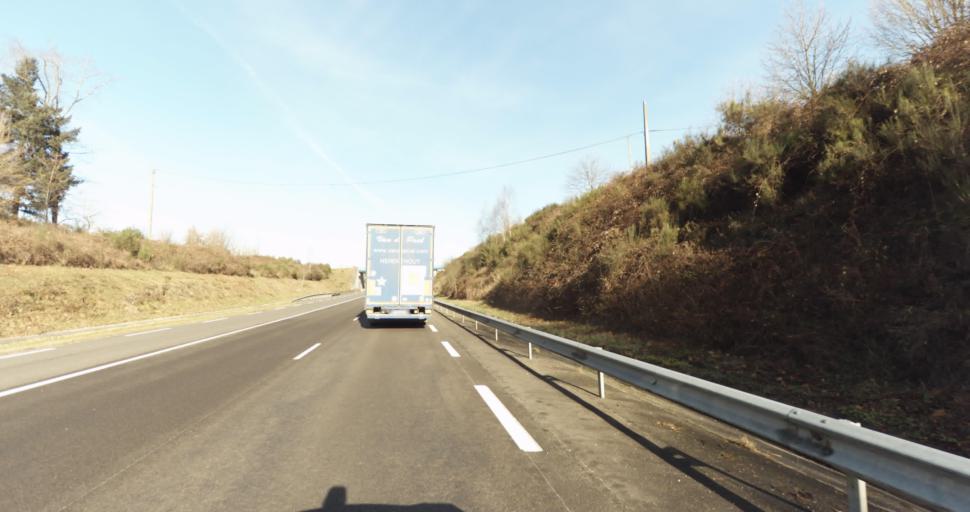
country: FR
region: Limousin
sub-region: Departement de la Haute-Vienne
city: Aixe-sur-Vienne
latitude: 45.8338
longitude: 1.1480
